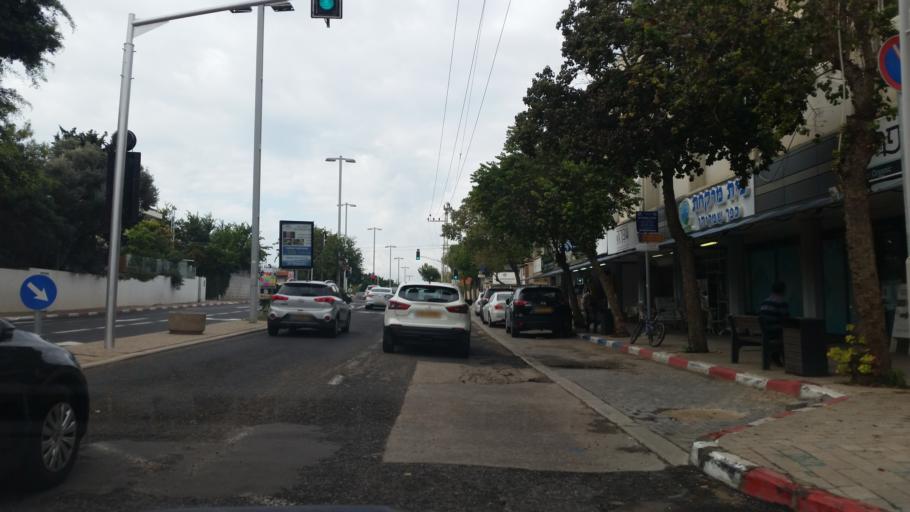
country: IL
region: Tel Aviv
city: Kefar Shemaryahu
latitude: 32.1797
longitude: 34.8194
